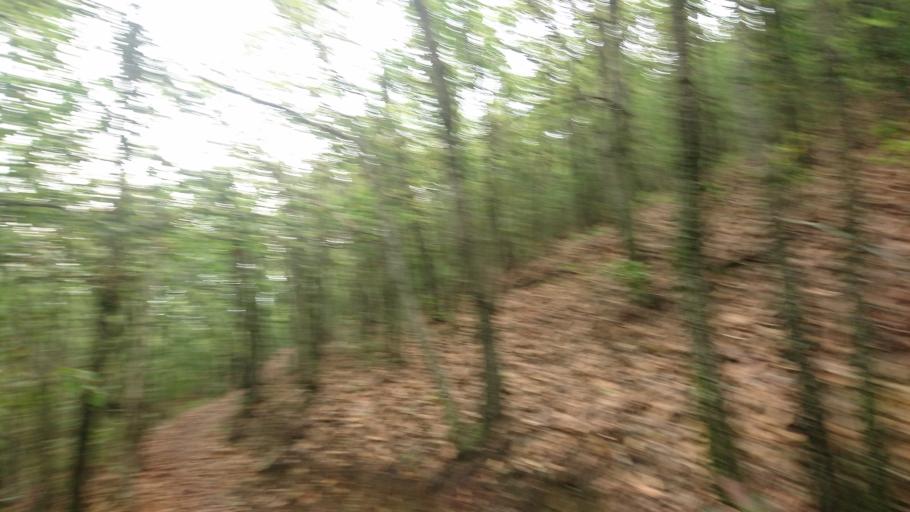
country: MX
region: Nuevo Leon
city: Garza Garcia
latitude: 25.6015
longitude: -100.3372
